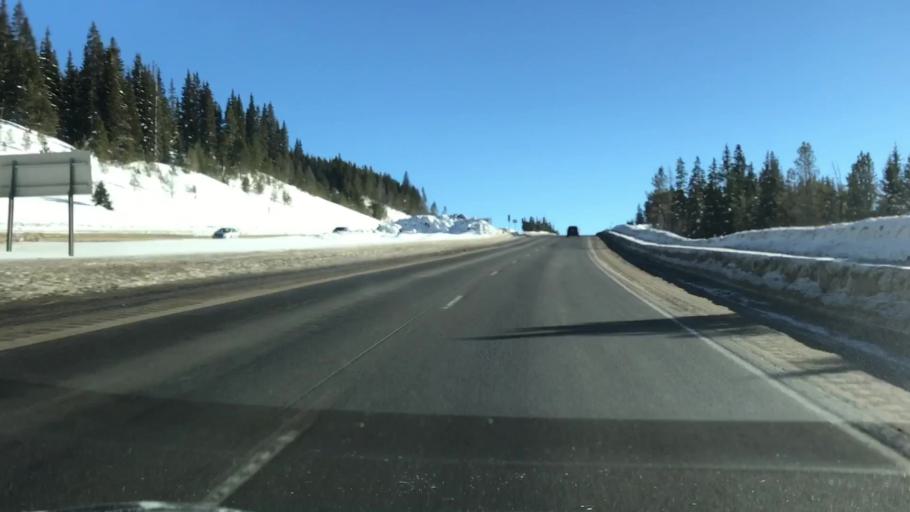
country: US
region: Colorado
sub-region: Summit County
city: Frisco
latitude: 39.5478
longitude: -106.2204
